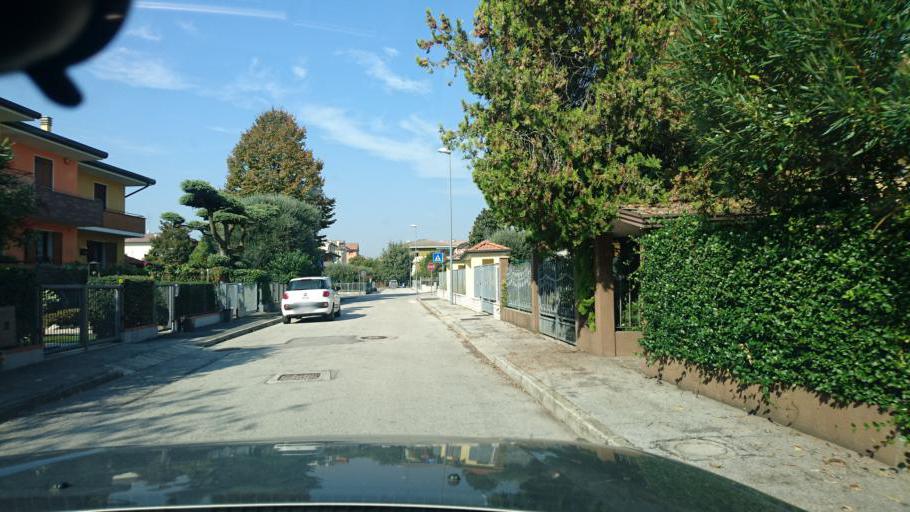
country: IT
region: Veneto
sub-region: Provincia di Padova
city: Mestrino
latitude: 45.4382
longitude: 11.7608
